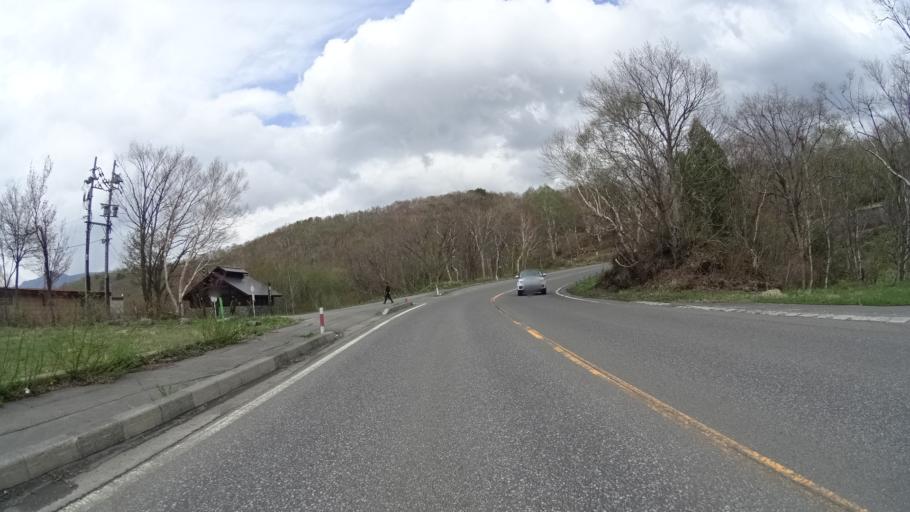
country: JP
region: Nagano
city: Nakano
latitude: 36.7190
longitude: 138.4857
